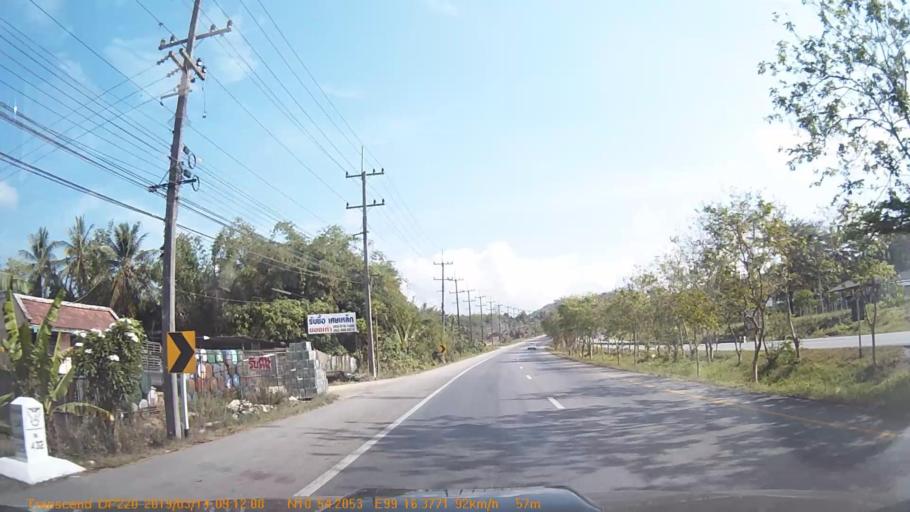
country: TH
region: Chumphon
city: Pathio
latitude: 10.9043
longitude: 99.2732
